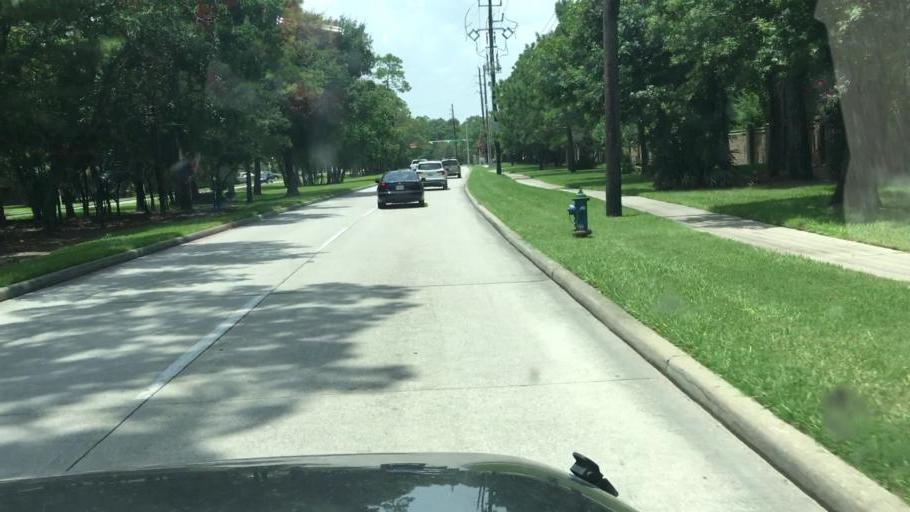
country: US
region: Texas
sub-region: Harris County
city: Atascocita
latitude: 29.9247
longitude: -95.1856
